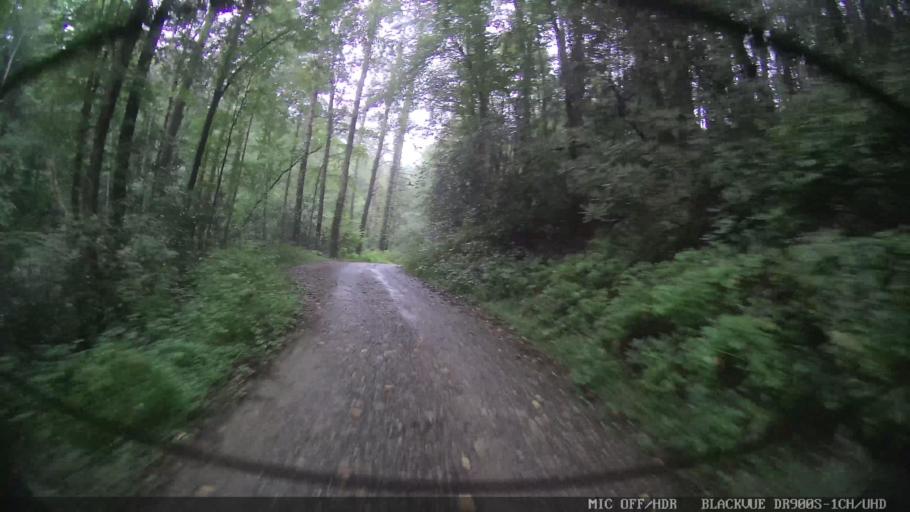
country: US
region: Georgia
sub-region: Gilmer County
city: Ellijay
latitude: 34.8108
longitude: -84.5589
